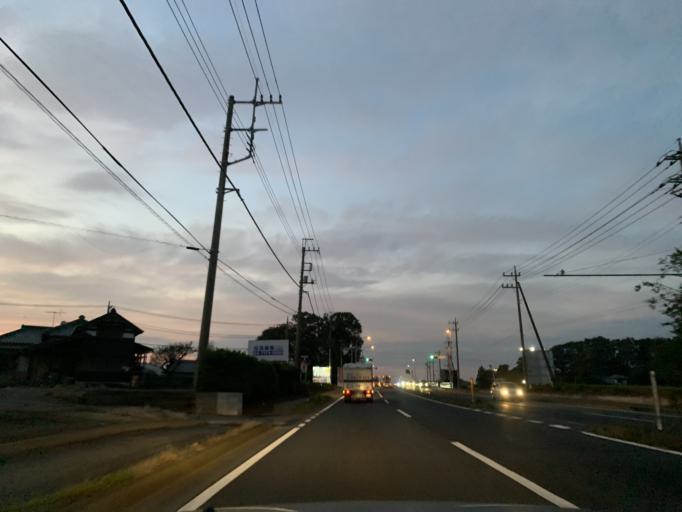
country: JP
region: Chiba
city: Nagareyama
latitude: 35.9146
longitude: 139.9292
